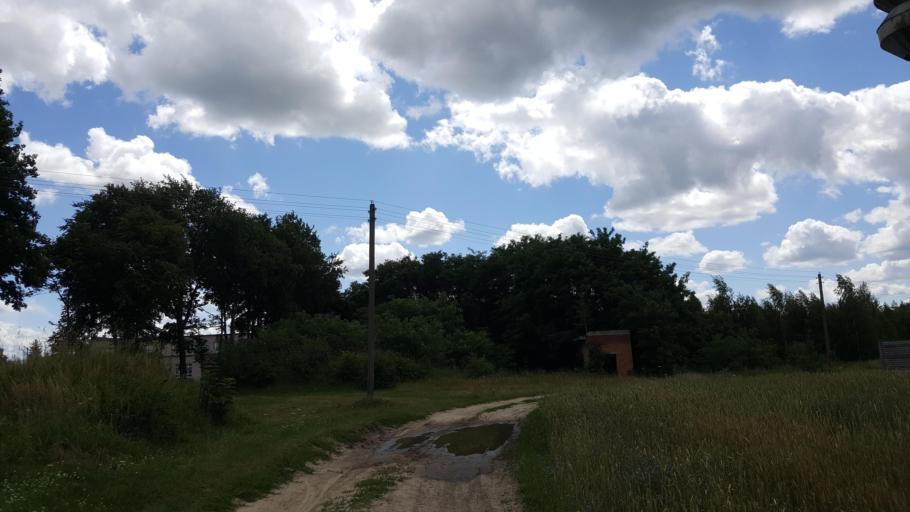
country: BY
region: Brest
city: Kamyanyets
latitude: 52.3214
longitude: 23.9302
